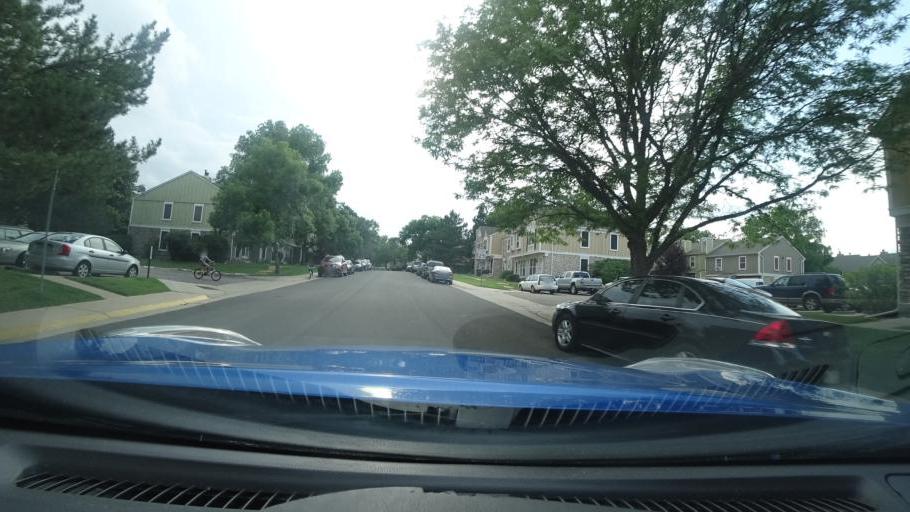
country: US
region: Colorado
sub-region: Adams County
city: Aurora
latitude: 39.6929
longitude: -104.8066
